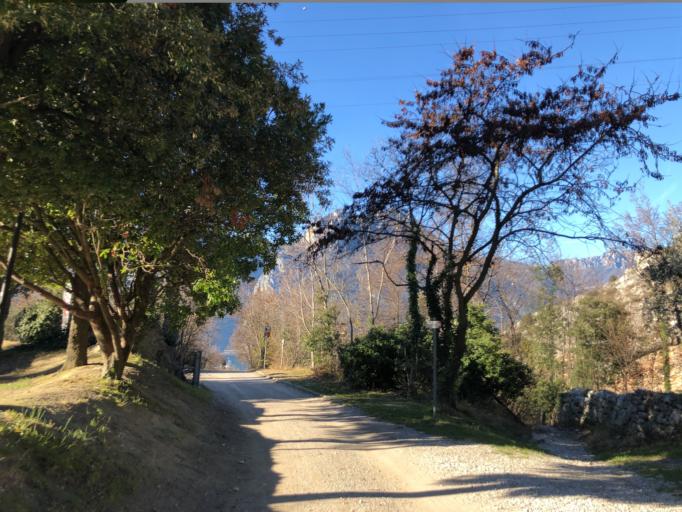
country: IT
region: Trentino-Alto Adige
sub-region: Provincia di Trento
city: Torbole sul Garda
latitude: 45.8660
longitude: 10.8821
